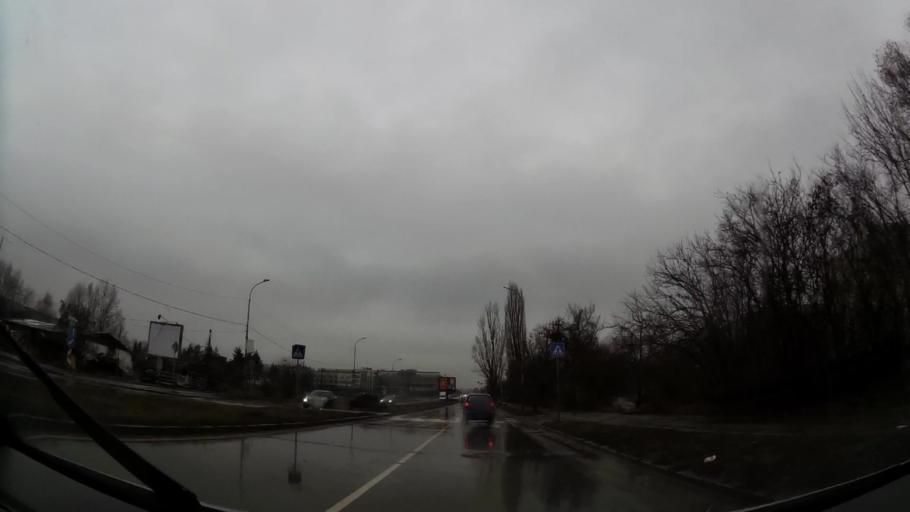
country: BG
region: Sofia-Capital
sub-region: Stolichna Obshtina
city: Sofia
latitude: 42.6516
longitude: 23.3553
